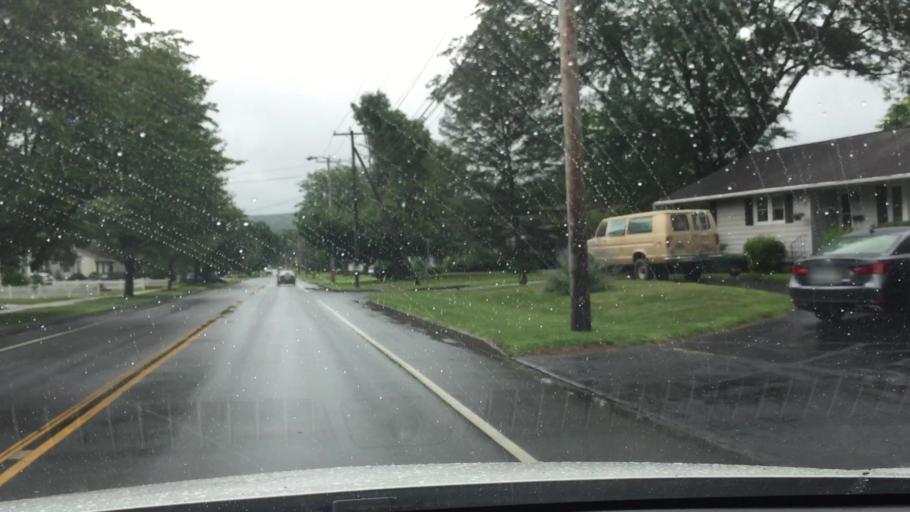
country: US
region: Massachusetts
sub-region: Berkshire County
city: Pittsfield
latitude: 42.4367
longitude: -73.2216
